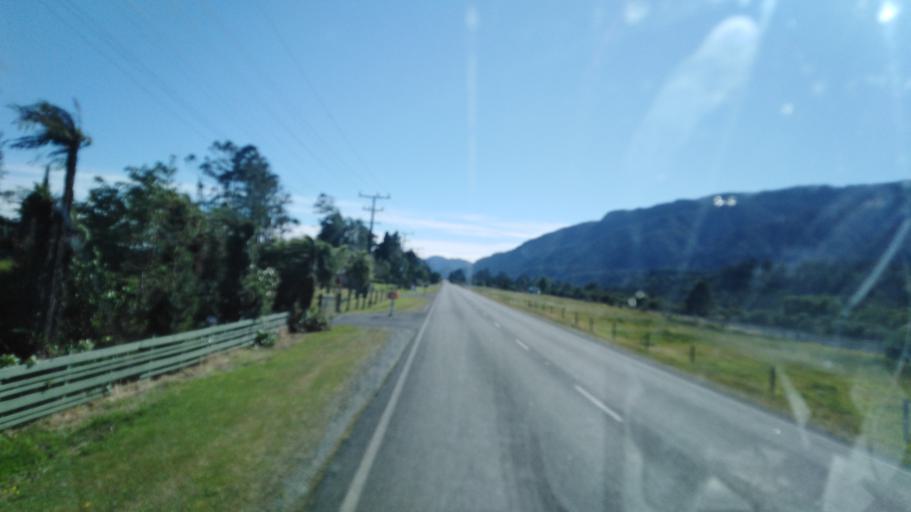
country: NZ
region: West Coast
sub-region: Buller District
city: Westport
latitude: -41.6759
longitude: 171.7984
